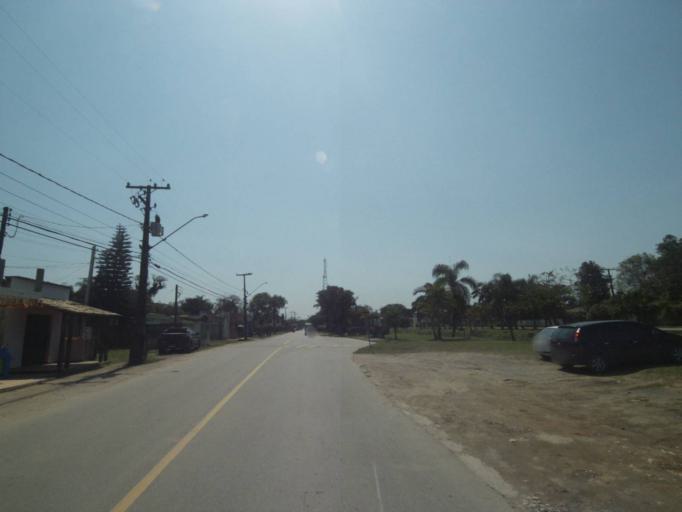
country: BR
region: Parana
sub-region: Paranagua
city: Paranagua
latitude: -25.5573
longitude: -48.6272
